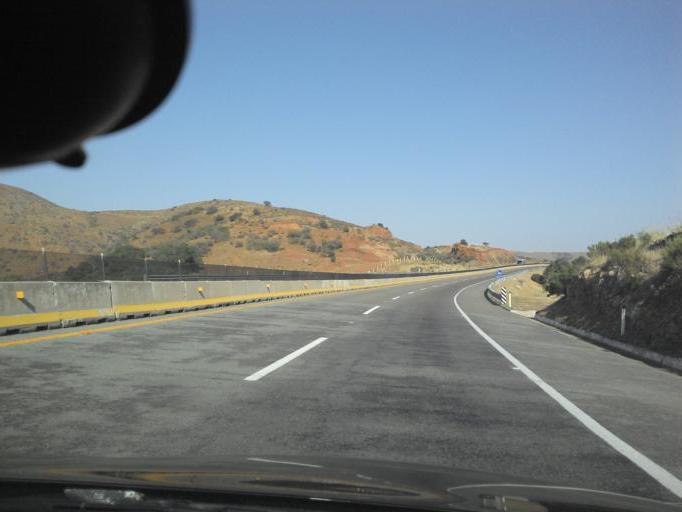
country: MX
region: Baja California
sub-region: Tijuana
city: El Nino
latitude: 32.5493
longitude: -116.7998
